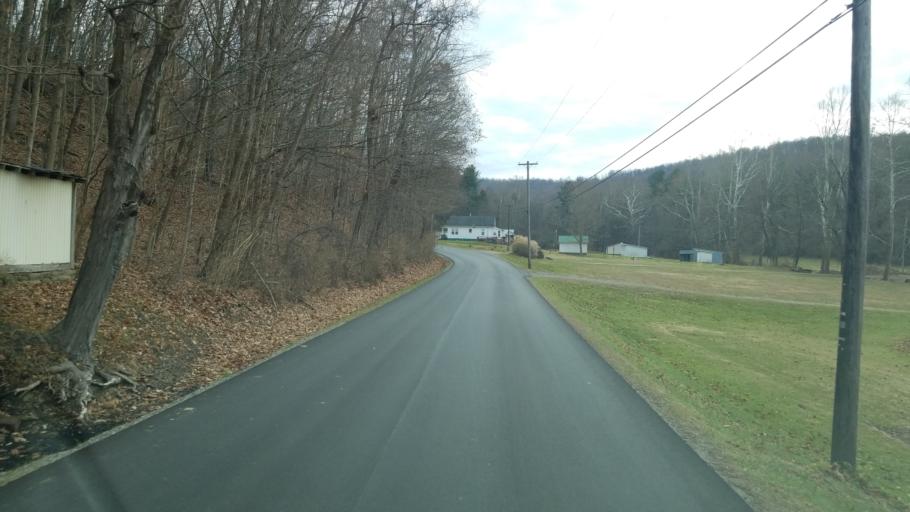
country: US
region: Ohio
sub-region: Highland County
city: Greenfield
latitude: 39.2171
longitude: -83.2690
